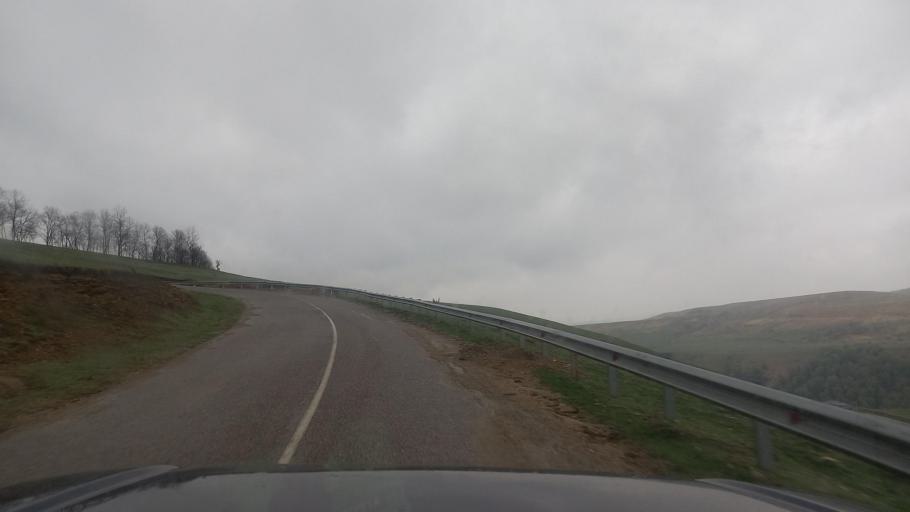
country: RU
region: Stavropol'skiy
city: Nezhinskiy
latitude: 43.8627
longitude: 42.6522
